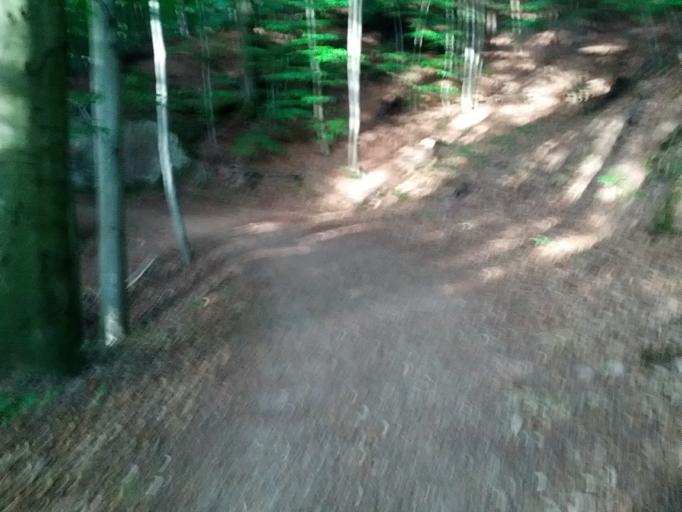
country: DE
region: Thuringia
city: Eisenach
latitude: 50.9501
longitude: 10.3305
